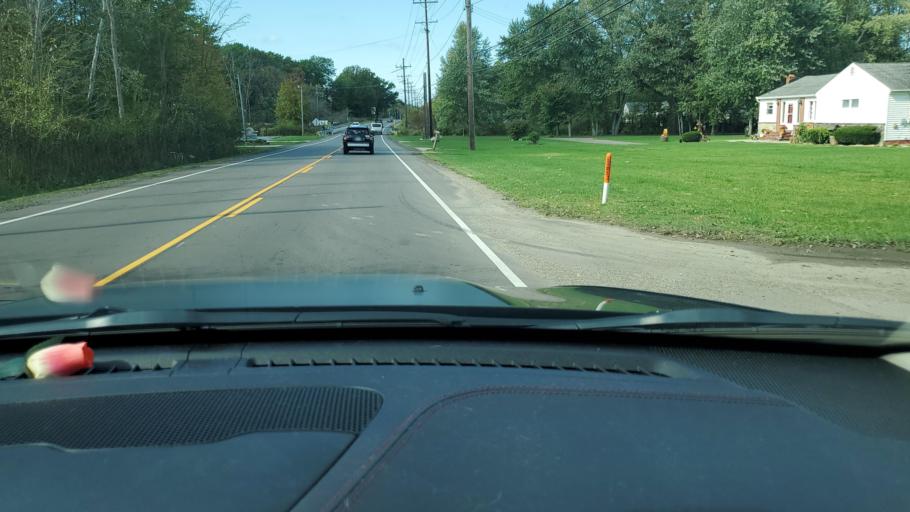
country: US
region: Ohio
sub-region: Trumbull County
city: Warren
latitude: 41.2655
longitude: -80.8163
